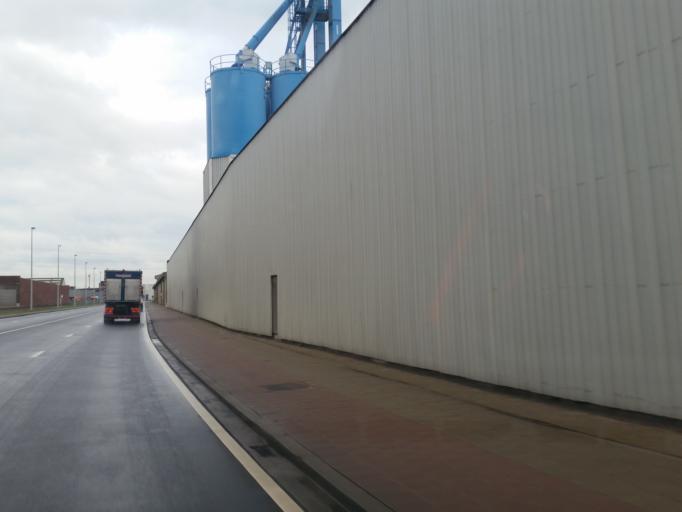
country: BE
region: Flanders
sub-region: Provincie Antwerpen
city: Antwerpen
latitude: 51.2611
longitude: 4.4082
